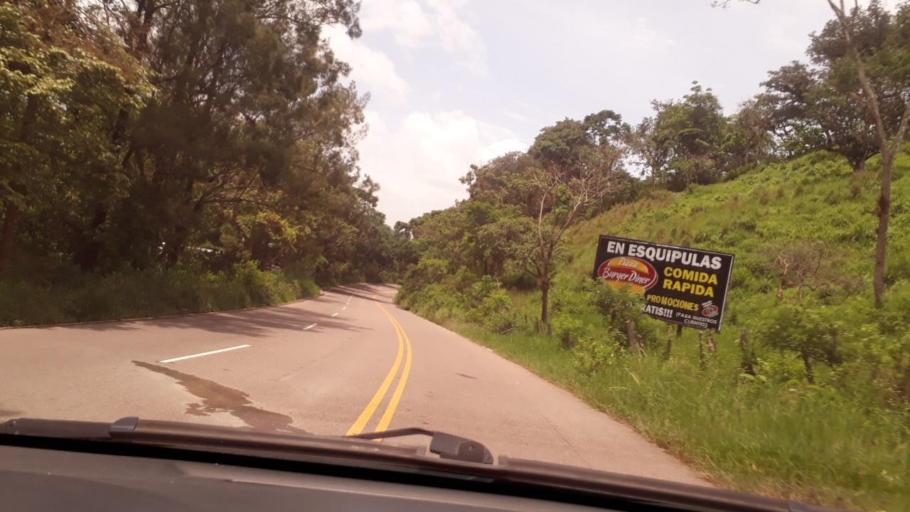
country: GT
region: Chiquimula
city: Esquipulas
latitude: 14.5509
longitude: -89.3892
